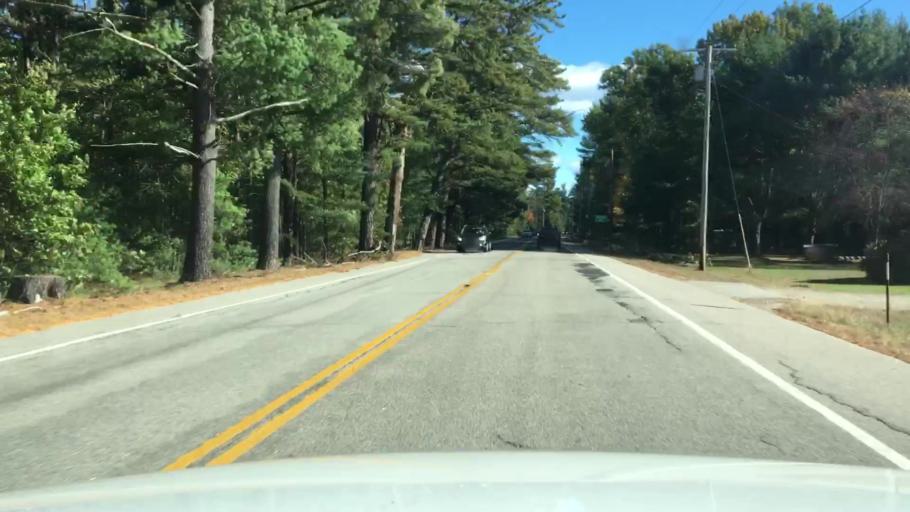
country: US
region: Maine
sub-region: York County
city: South Sanford
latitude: 43.3784
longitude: -70.6834
